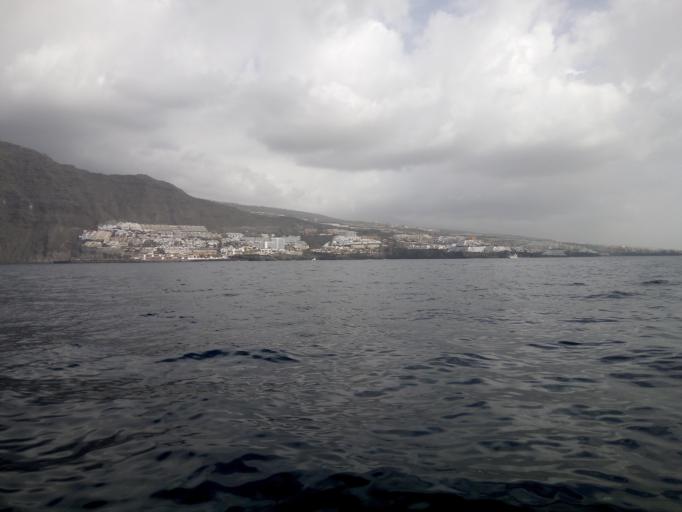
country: ES
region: Canary Islands
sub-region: Provincia de Santa Cruz de Tenerife
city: Santiago del Teide
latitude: 28.2487
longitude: -16.8564
